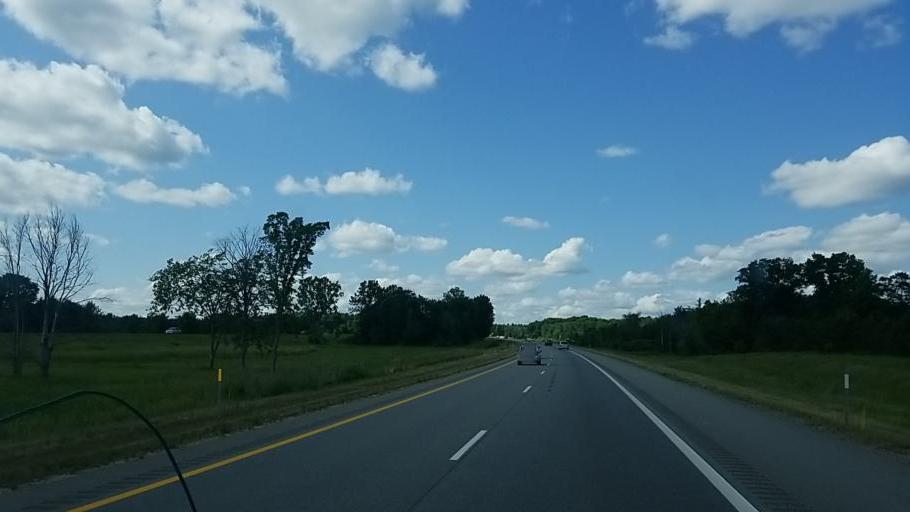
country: US
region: Michigan
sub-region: Mecosta County
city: Big Rapids
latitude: 43.6221
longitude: -85.4986
